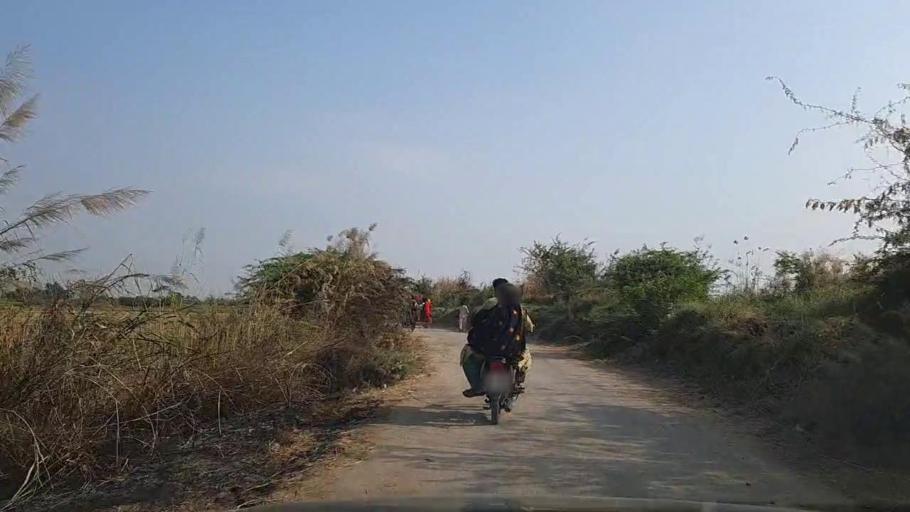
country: PK
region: Sindh
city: Thatta
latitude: 24.6488
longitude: 67.9258
